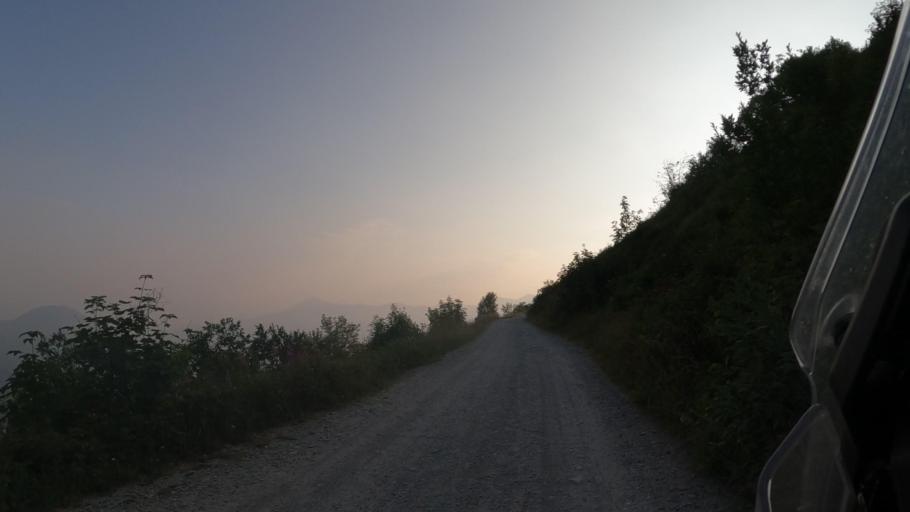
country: IT
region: Piedmont
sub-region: Provincia di Cuneo
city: Limone Piemonte
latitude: 44.1524
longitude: 7.5735
